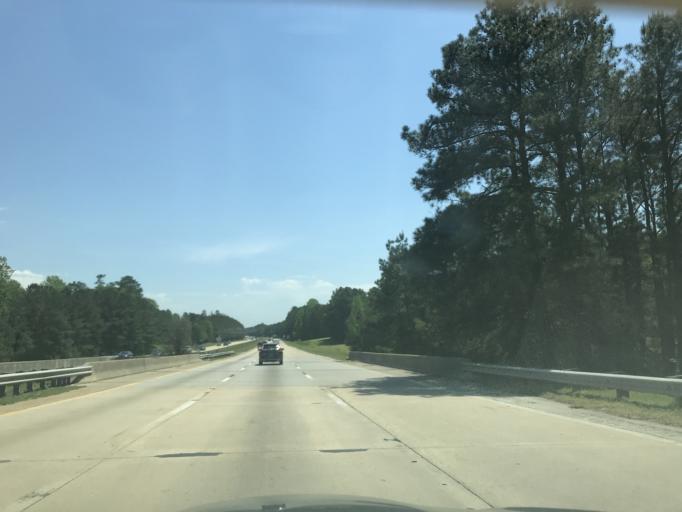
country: US
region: North Carolina
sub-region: Wake County
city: Garner
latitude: 35.6918
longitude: -78.5734
